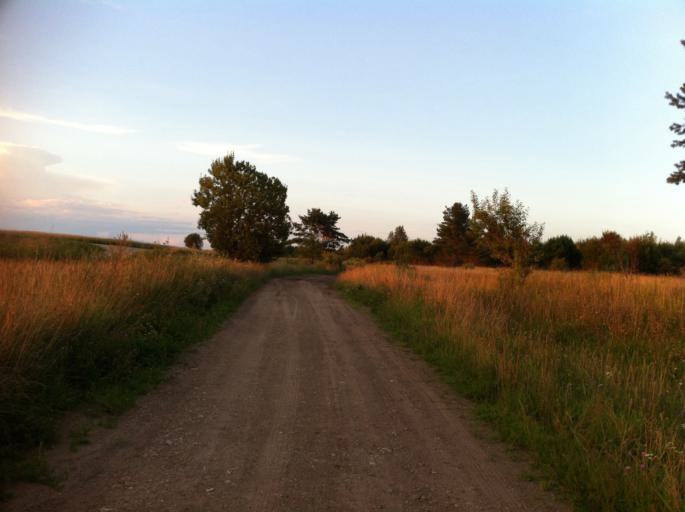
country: RU
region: Pskov
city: Izborsk
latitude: 57.8224
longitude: 27.9662
